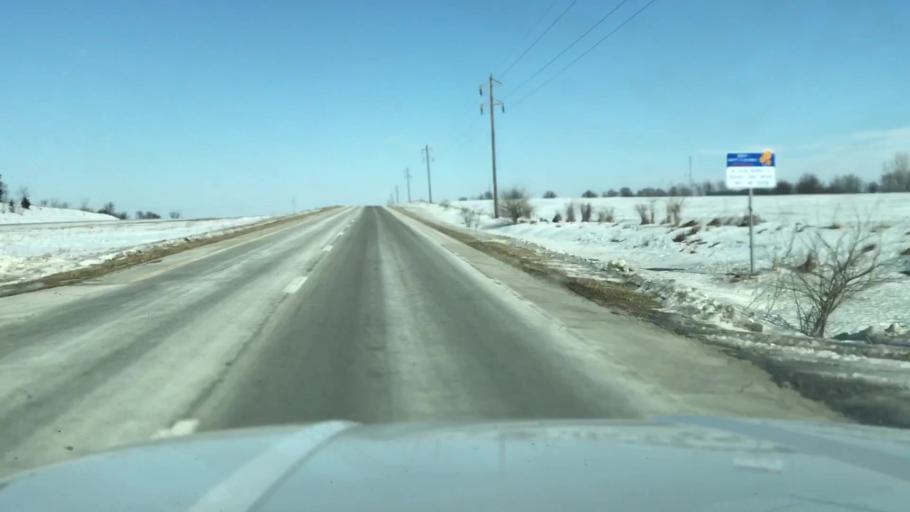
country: US
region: Missouri
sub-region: Nodaway County
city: Maryville
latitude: 40.1571
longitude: -94.8690
